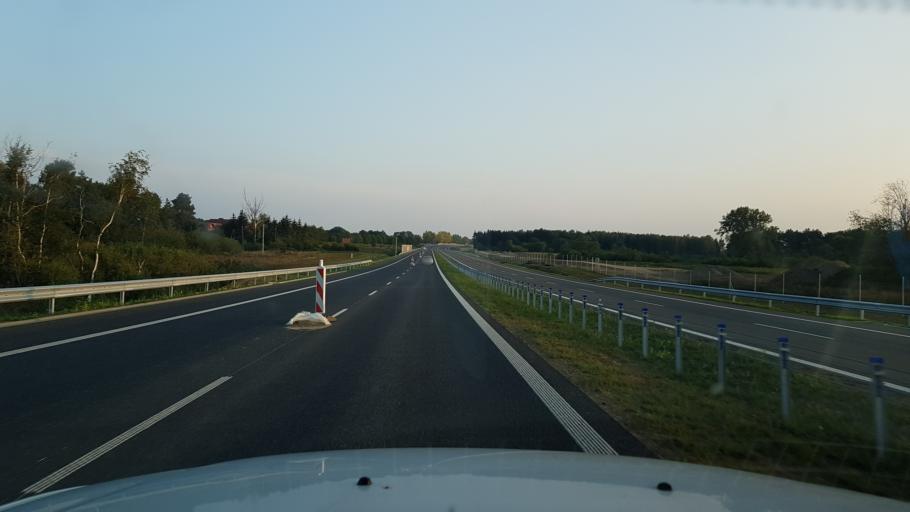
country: PL
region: West Pomeranian Voivodeship
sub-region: Powiat gryficki
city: Ploty
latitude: 53.7943
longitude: 15.2527
